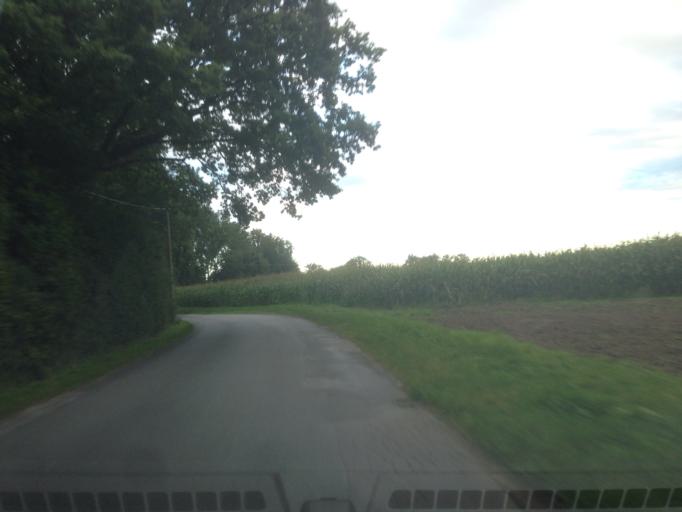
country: DE
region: North Rhine-Westphalia
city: Olfen
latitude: 51.7254
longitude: 7.3742
